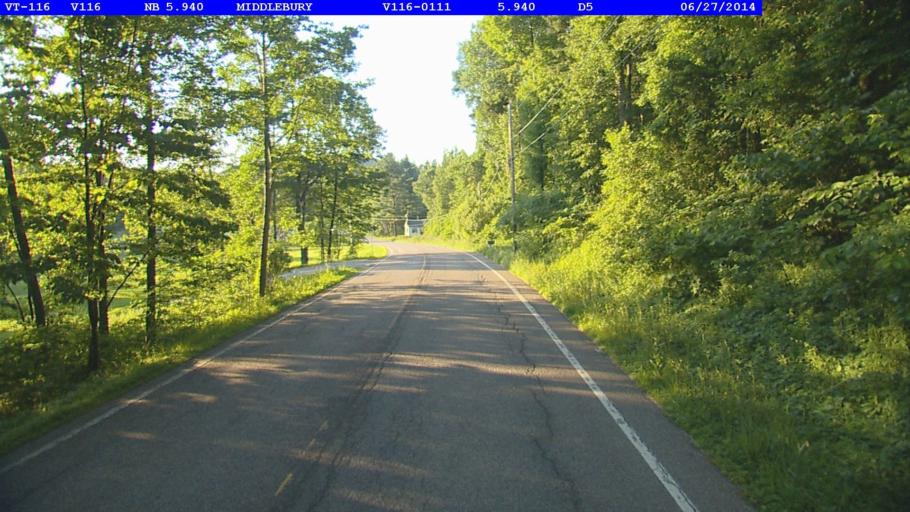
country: US
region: Vermont
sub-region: Addison County
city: Middlebury (village)
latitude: 44.0456
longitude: -73.0904
